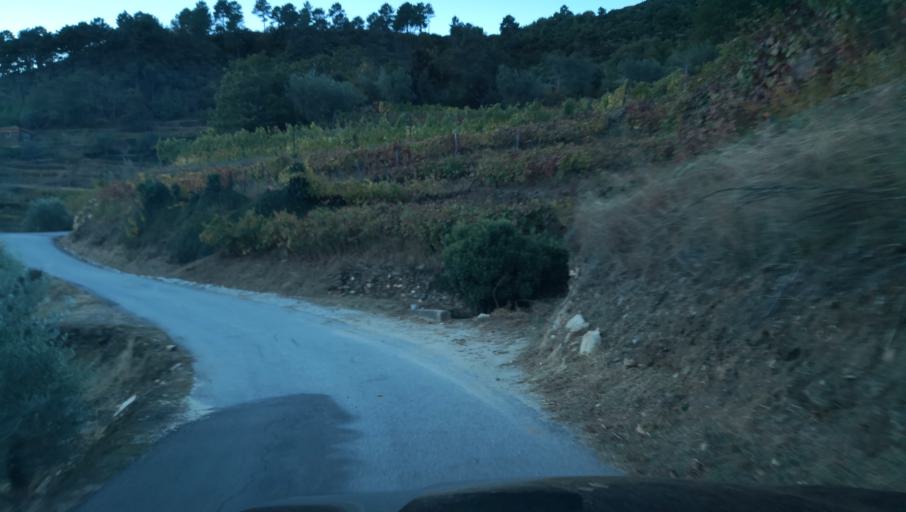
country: PT
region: Vila Real
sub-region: Santa Marta de Penaguiao
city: Santa Marta de Penaguiao
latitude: 41.2580
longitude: -7.8177
